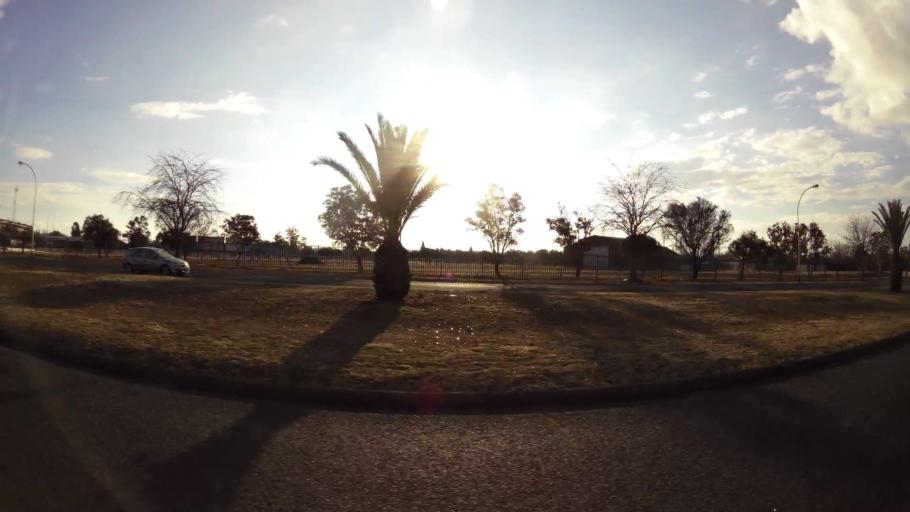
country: ZA
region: Orange Free State
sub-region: Mangaung Metropolitan Municipality
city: Bloemfontein
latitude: -29.1488
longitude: 26.1871
